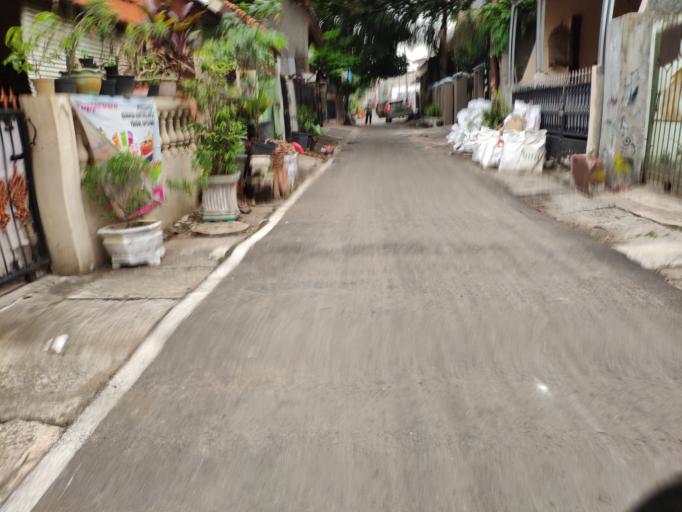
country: ID
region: Jakarta Raya
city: Jakarta
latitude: -6.2001
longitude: 106.8660
